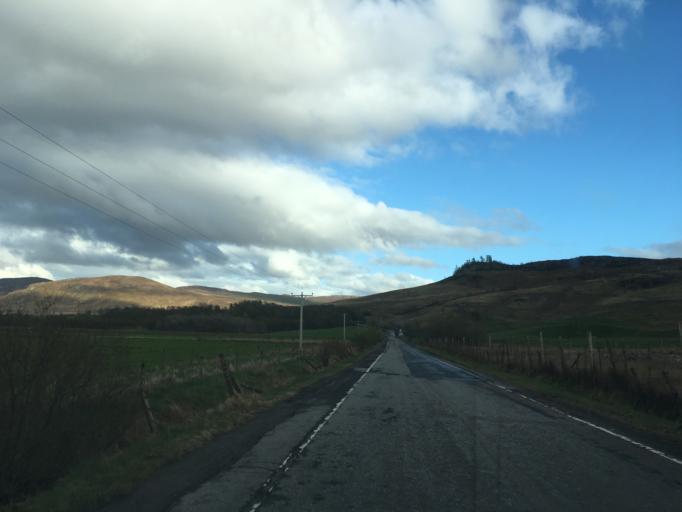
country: GB
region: Scotland
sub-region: Highland
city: Kingussie
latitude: 57.0120
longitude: -4.2707
